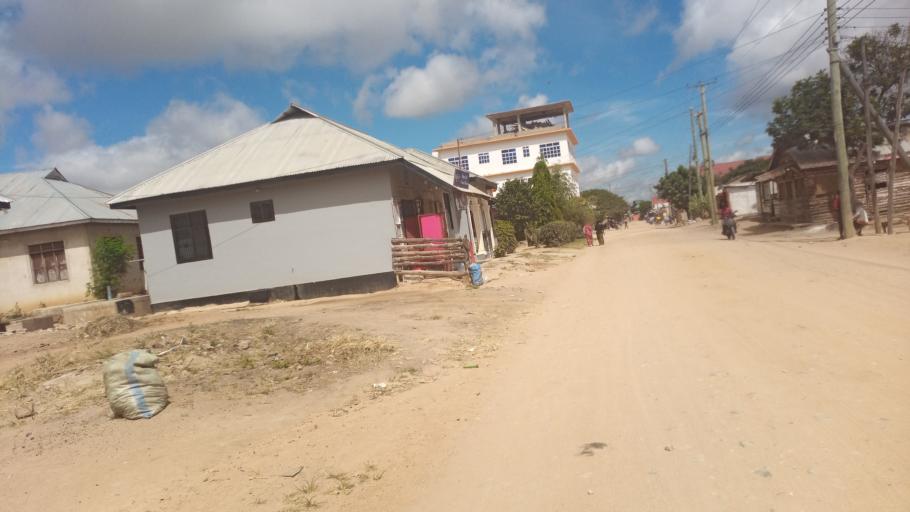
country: TZ
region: Dodoma
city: Kisasa
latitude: -6.1754
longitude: 35.7684
